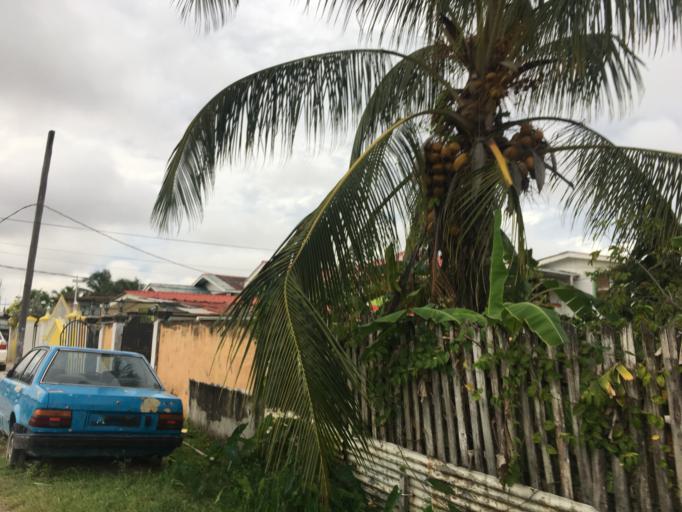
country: GY
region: Demerara-Mahaica
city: Georgetown
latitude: 6.8054
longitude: -58.1167
